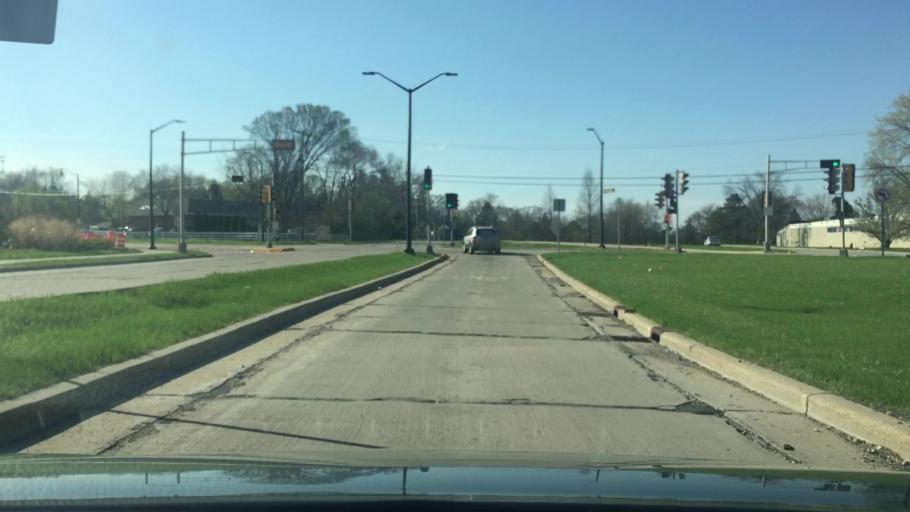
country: US
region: Wisconsin
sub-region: Milwaukee County
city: Brown Deer
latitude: 43.1627
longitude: -87.9628
